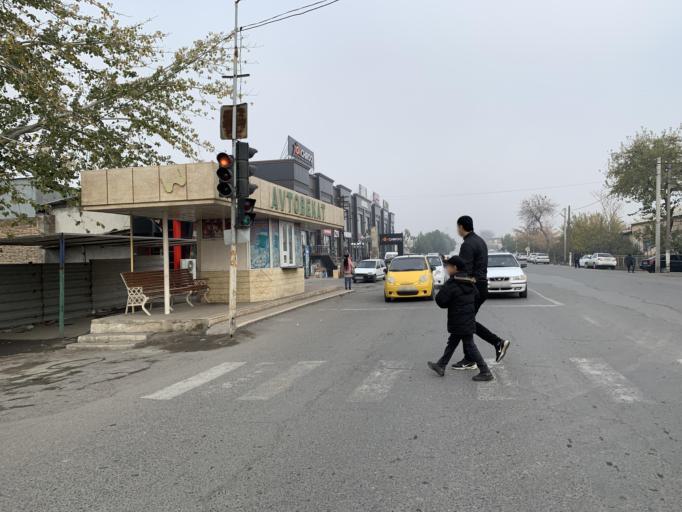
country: UZ
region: Fergana
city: Qo`qon
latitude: 40.5477
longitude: 70.9576
